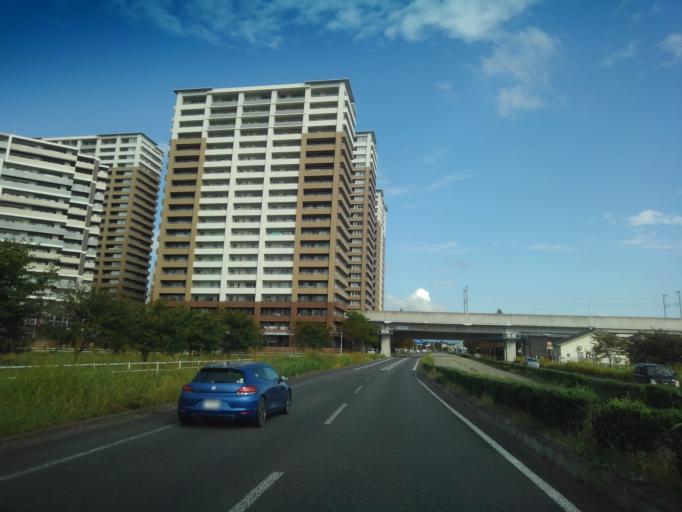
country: JP
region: Ibaraki
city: Naka
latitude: 36.0806
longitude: 140.0860
